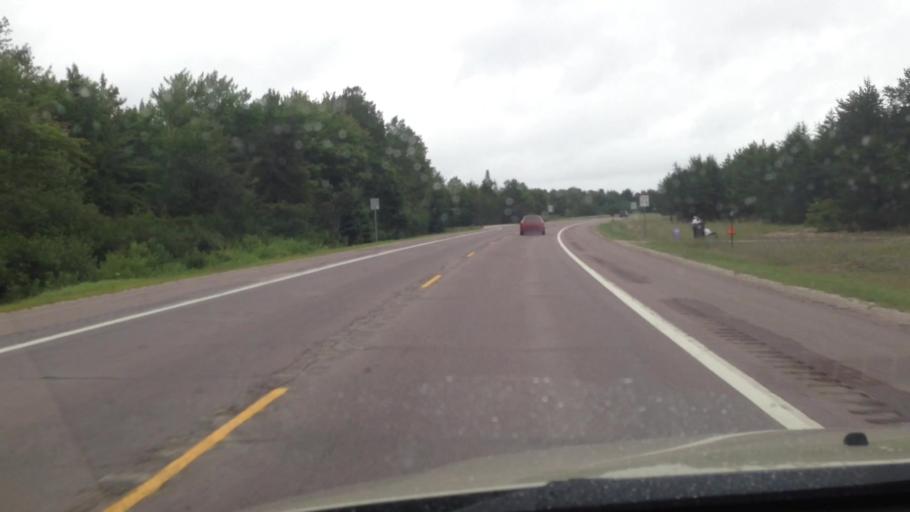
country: US
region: Michigan
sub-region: Schoolcraft County
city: Manistique
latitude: 45.9412
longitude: -86.2813
